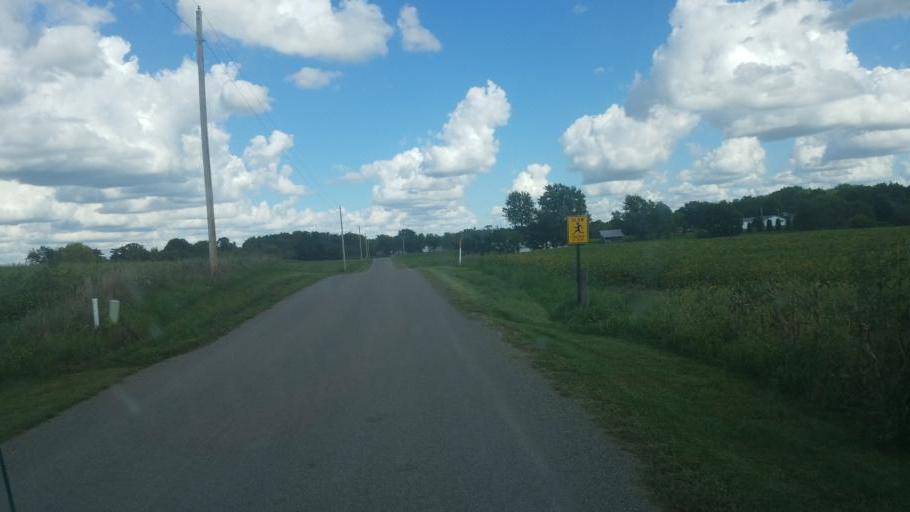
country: US
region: Ohio
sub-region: Hardin County
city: Kenton
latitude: 40.5488
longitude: -83.5405
